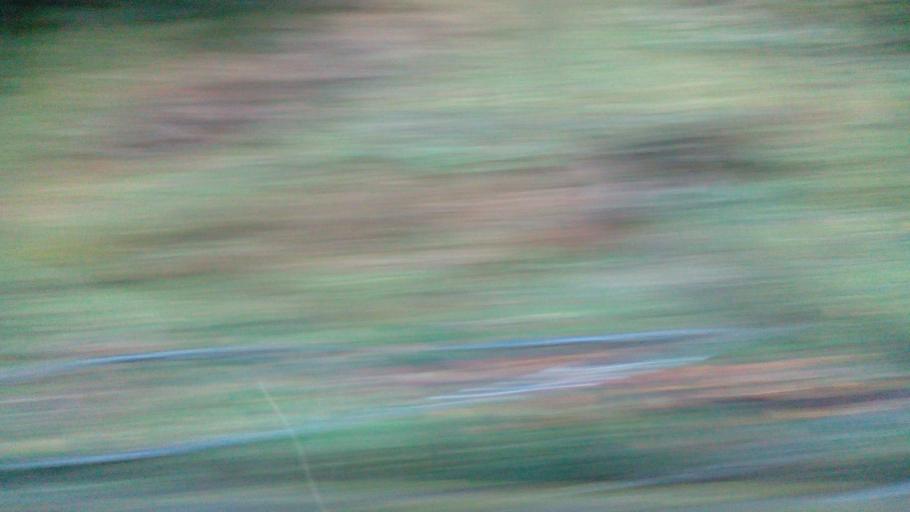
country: TW
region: Taiwan
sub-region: Hualien
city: Hualian
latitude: 24.3475
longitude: 121.3200
